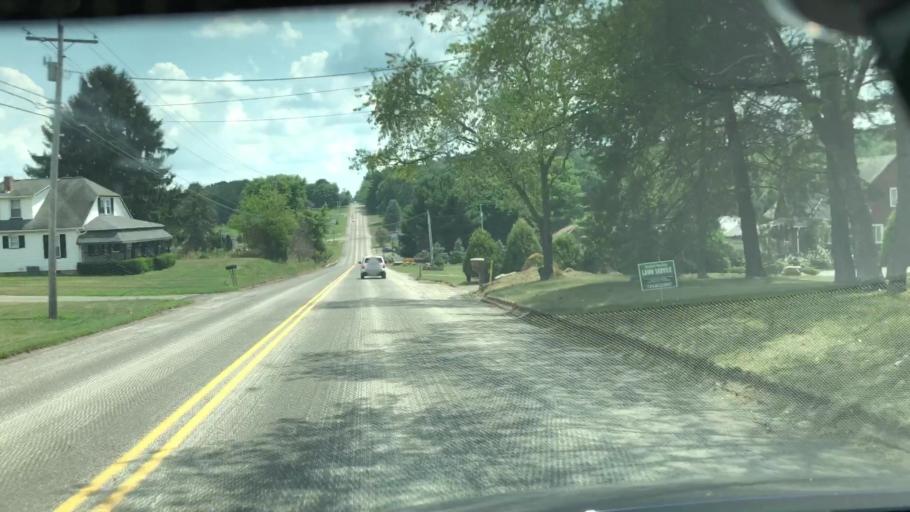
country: US
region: Pennsylvania
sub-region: Butler County
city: Saxonburg
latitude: 40.8040
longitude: -79.8277
